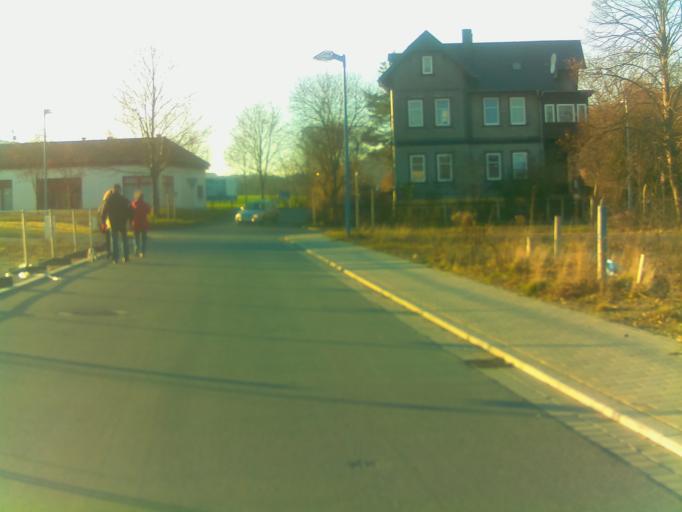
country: DE
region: Thuringia
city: Bad Blankenburg
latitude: 50.6855
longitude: 11.3057
